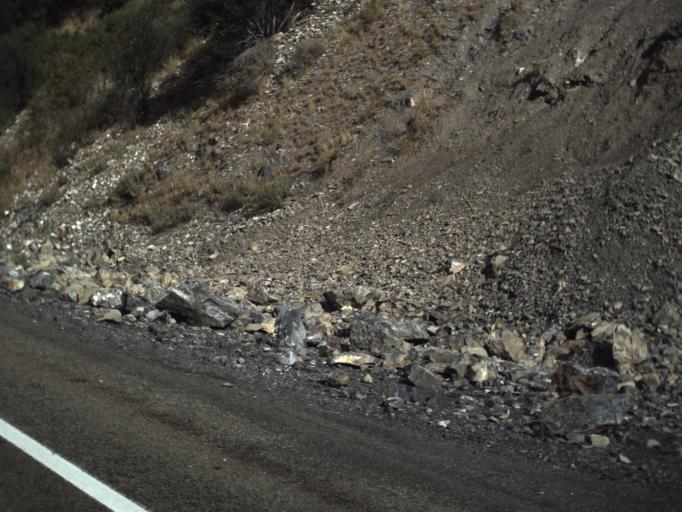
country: US
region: Utah
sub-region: Utah County
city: Orem
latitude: 40.3155
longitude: -111.6528
